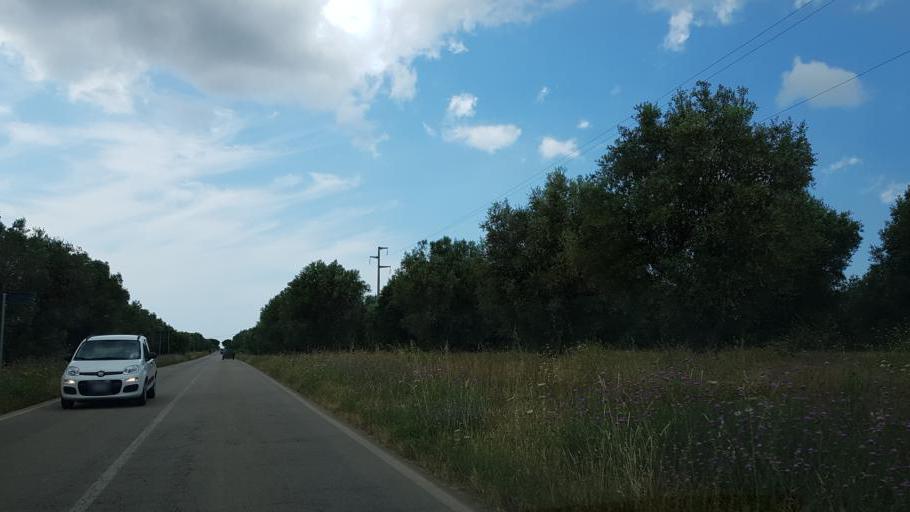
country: IT
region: Apulia
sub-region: Provincia di Brindisi
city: San Pancrazio Salentino
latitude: 40.3521
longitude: 17.8453
